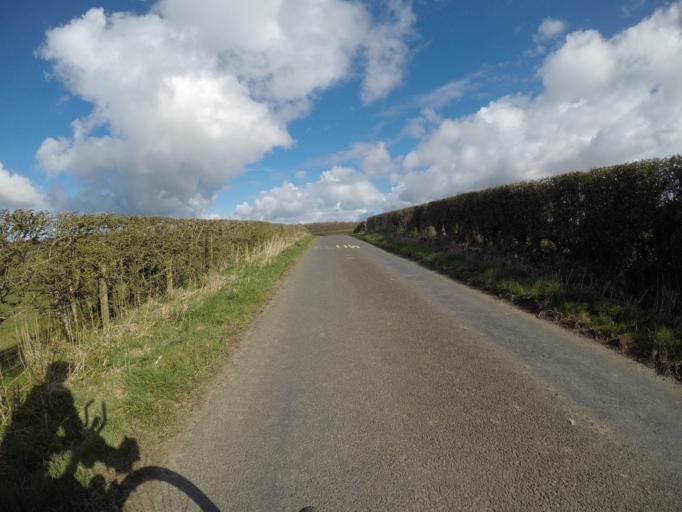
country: GB
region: Scotland
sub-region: North Ayrshire
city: Irvine
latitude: 55.6676
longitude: -4.6508
